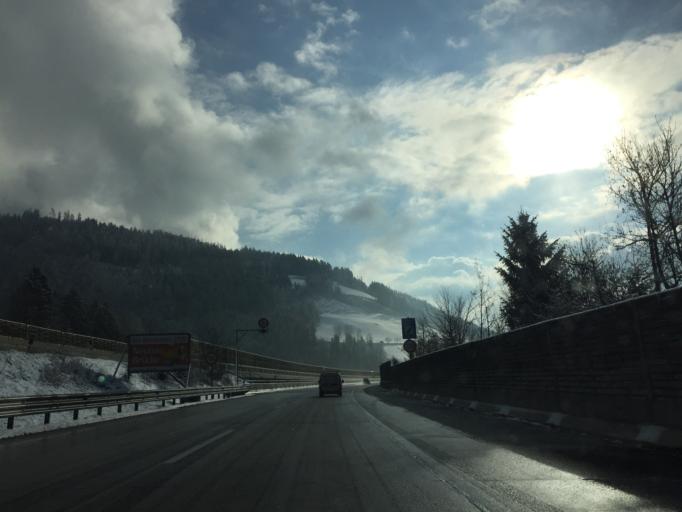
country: AT
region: Salzburg
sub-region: Politischer Bezirk Sankt Johann im Pongau
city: Huttau
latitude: 47.4297
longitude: 13.2908
